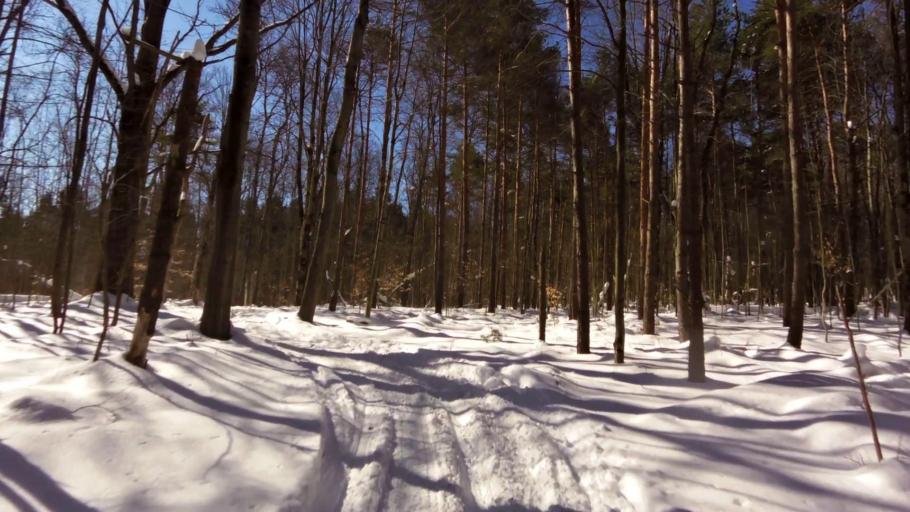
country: US
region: New York
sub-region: Allegany County
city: Cuba
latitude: 42.3227
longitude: -78.2758
